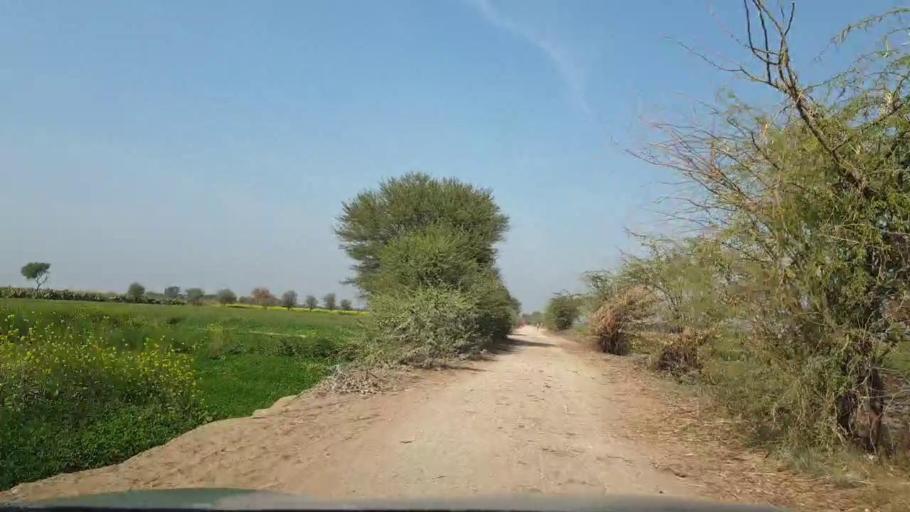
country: PK
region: Sindh
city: Berani
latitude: 25.7018
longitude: 68.7535
